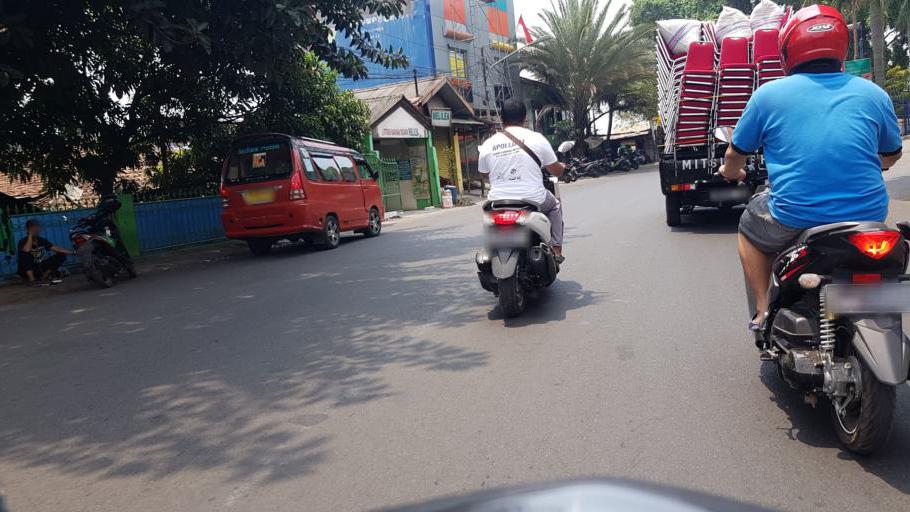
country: ID
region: West Java
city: Bekasi
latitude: -6.2835
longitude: 106.9104
